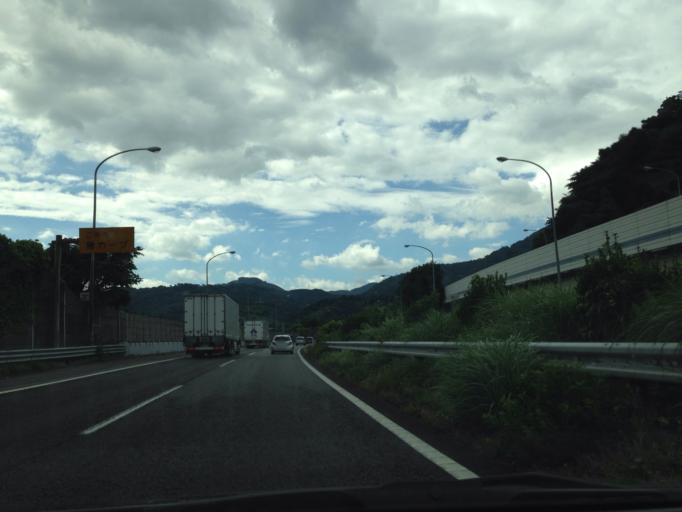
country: JP
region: Kanagawa
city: Odawara
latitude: 35.3603
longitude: 139.1051
